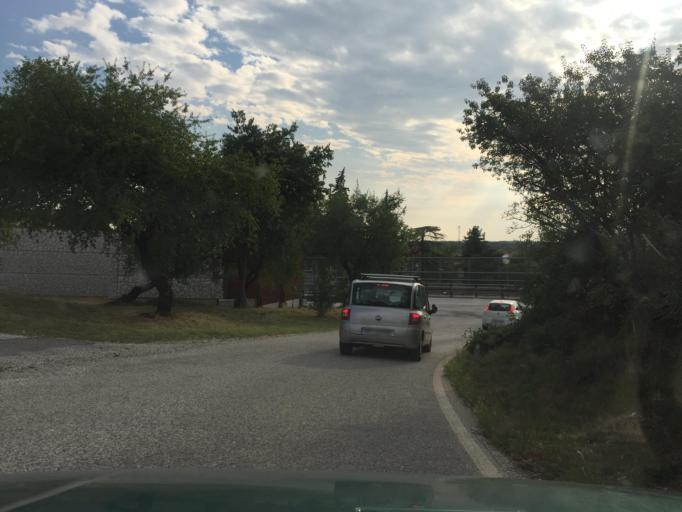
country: IT
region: Friuli Venezia Giulia
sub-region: Provincia di Trieste
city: Duino
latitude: 45.7912
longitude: 13.5914
